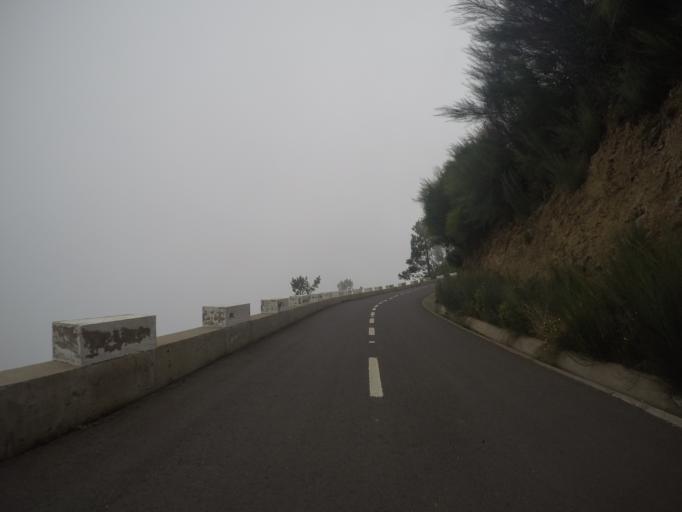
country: PT
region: Madeira
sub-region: Camara de Lobos
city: Curral das Freiras
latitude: 32.7064
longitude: -16.9557
